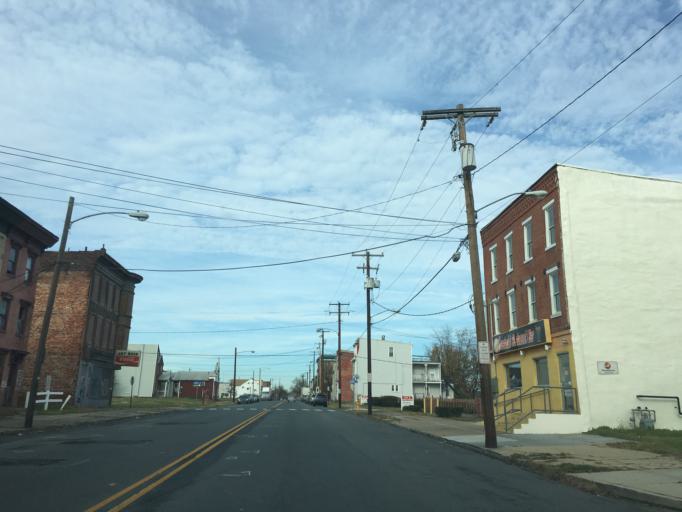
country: US
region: Pennsylvania
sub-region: Dauphin County
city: Harrisburg
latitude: 40.2740
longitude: -76.8870
